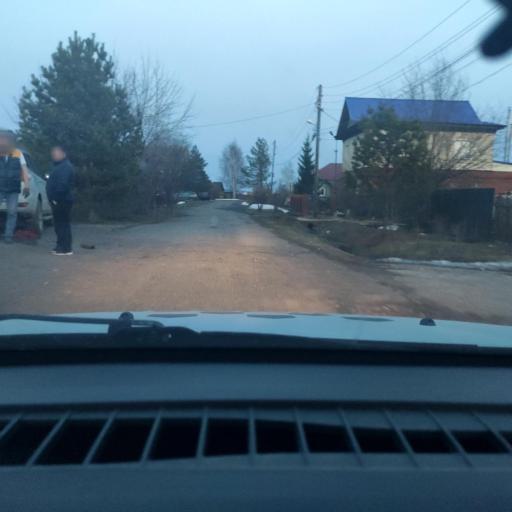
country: RU
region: Perm
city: Froly
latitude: 57.9089
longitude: 56.2068
